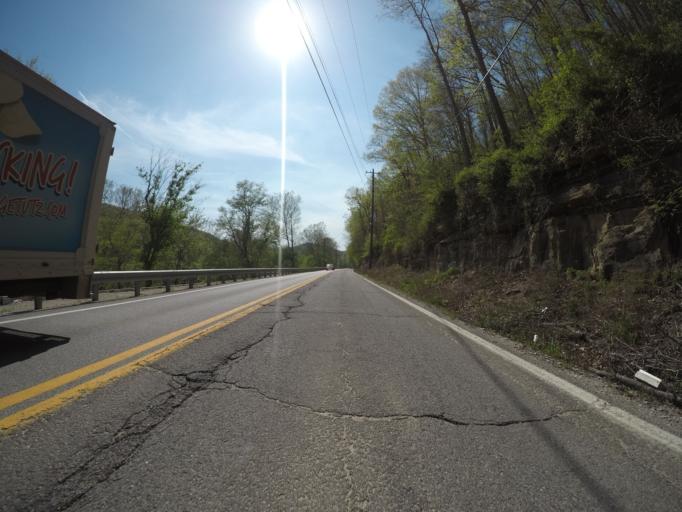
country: US
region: West Virginia
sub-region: Kanawha County
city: Clendenin
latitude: 38.4754
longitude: -81.3801
